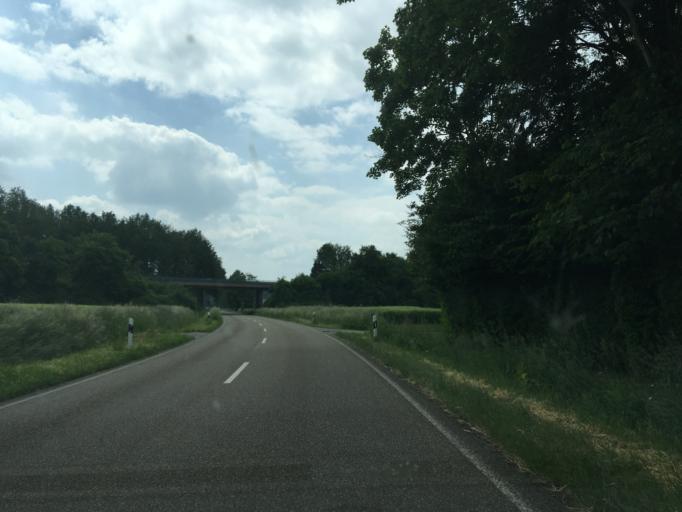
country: DE
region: North Rhine-Westphalia
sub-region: Regierungsbezirk Munster
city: Sudlohn
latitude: 51.9265
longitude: 6.8741
